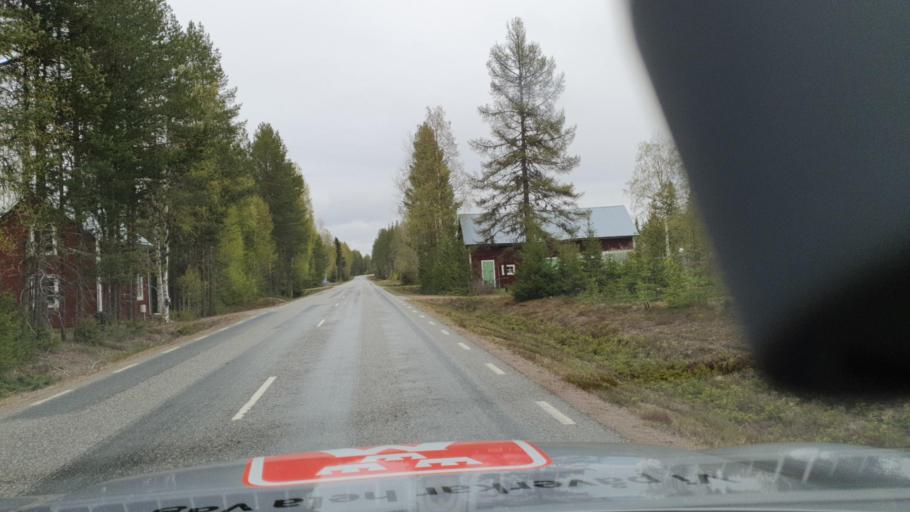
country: SE
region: Vaesternorrland
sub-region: Solleftea Kommun
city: As
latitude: 63.6836
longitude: 16.9630
